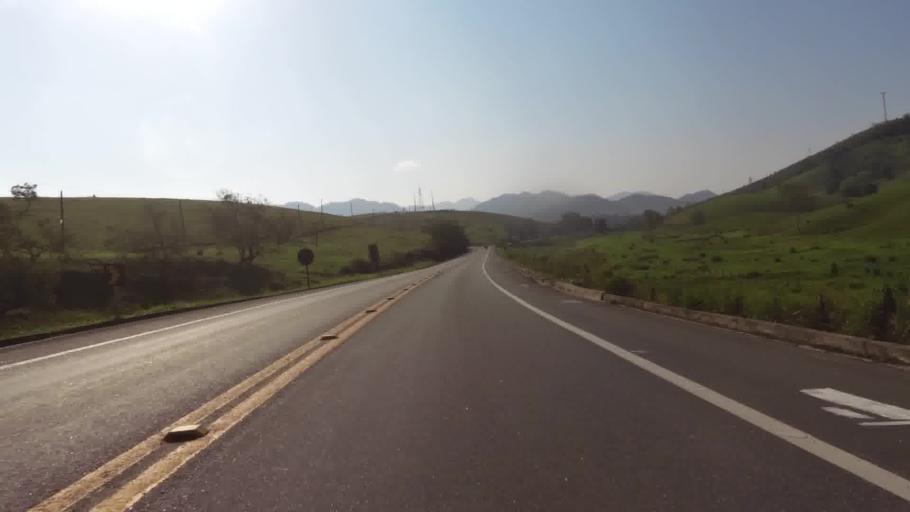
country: BR
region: Espirito Santo
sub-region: Iconha
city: Iconha
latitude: -20.7547
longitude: -40.7584
